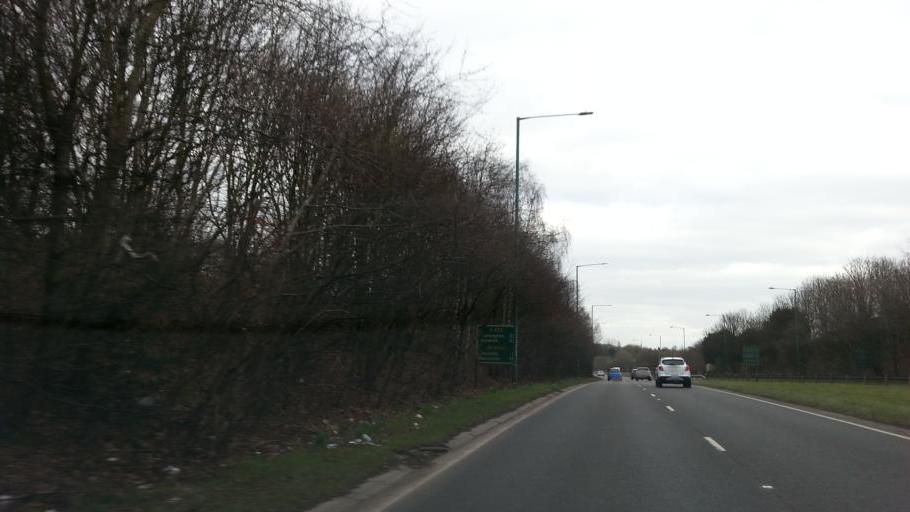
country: GB
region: England
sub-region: Warwickshire
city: Water Orton
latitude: 52.5083
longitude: -1.7905
